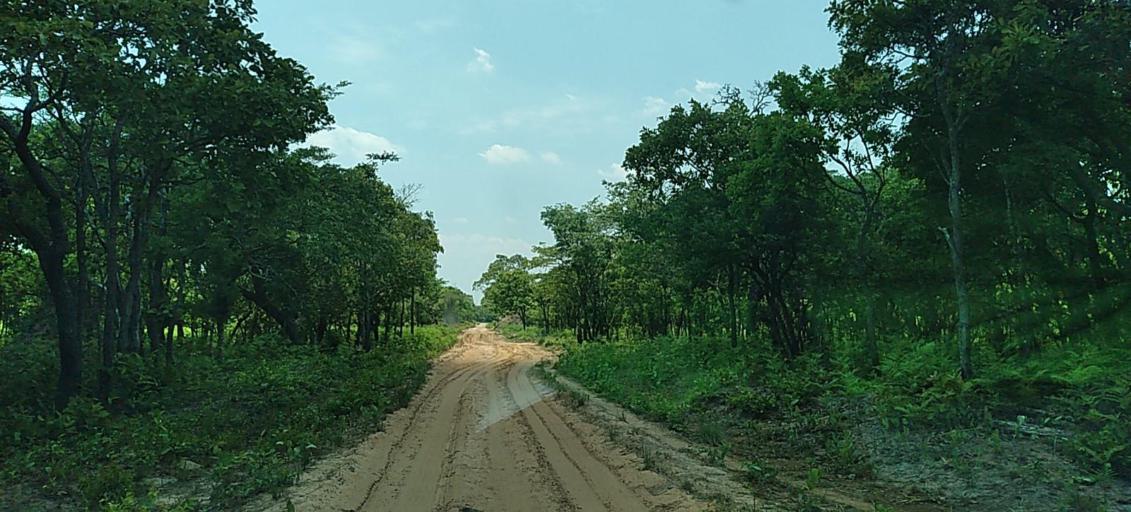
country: CD
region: Katanga
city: Kolwezi
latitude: -11.3469
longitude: 25.2156
